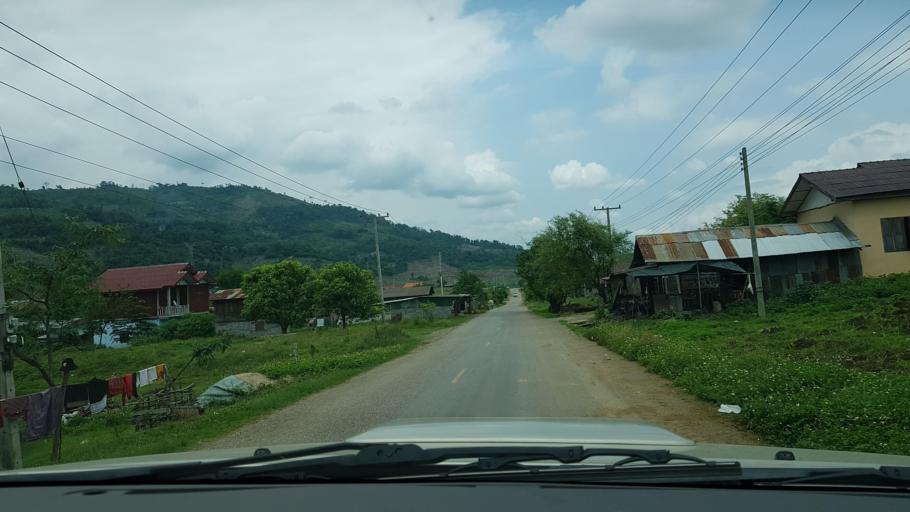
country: TH
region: Nan
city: Chaloem Phra Kiat
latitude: 19.9935
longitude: 101.2799
